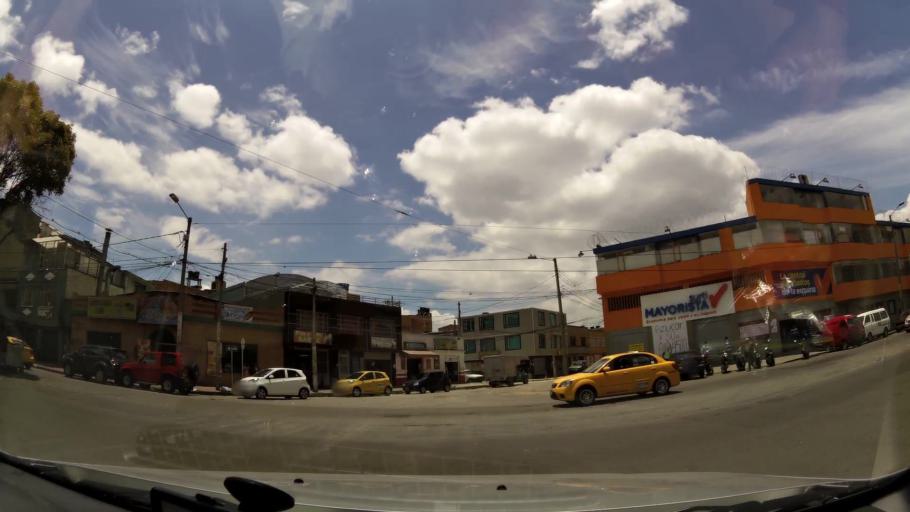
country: CO
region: Bogota D.C.
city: Bogota
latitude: 4.5916
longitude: -74.1041
